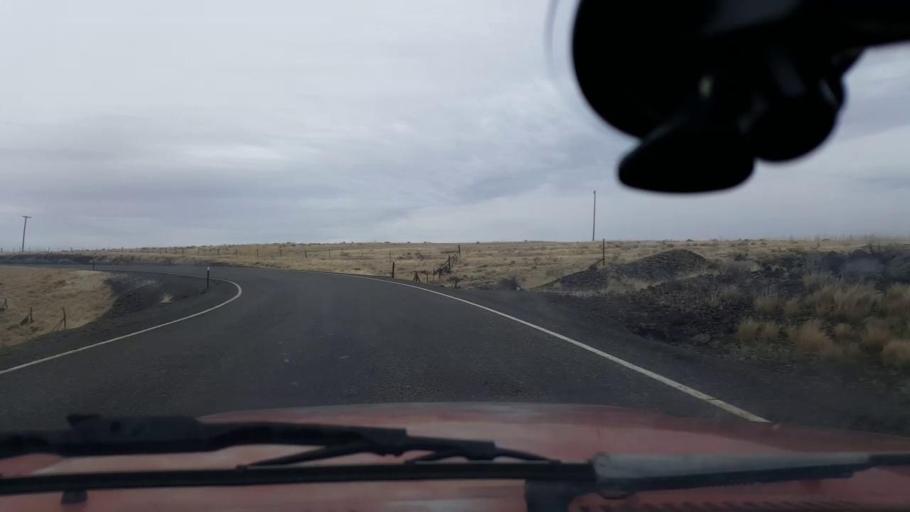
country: US
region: Washington
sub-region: Asotin County
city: Clarkston Heights-Vineland
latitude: 46.3227
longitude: -117.3536
